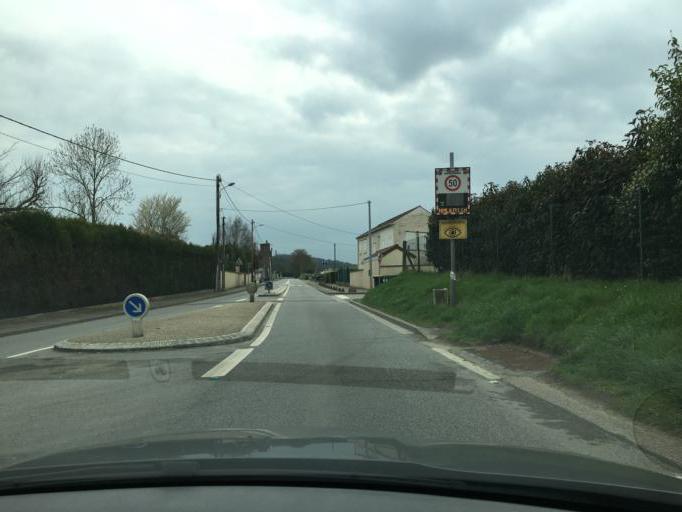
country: FR
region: Ile-de-France
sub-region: Departement des Yvelines
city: Mantes-la-Ville
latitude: 48.9601
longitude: 1.7082
